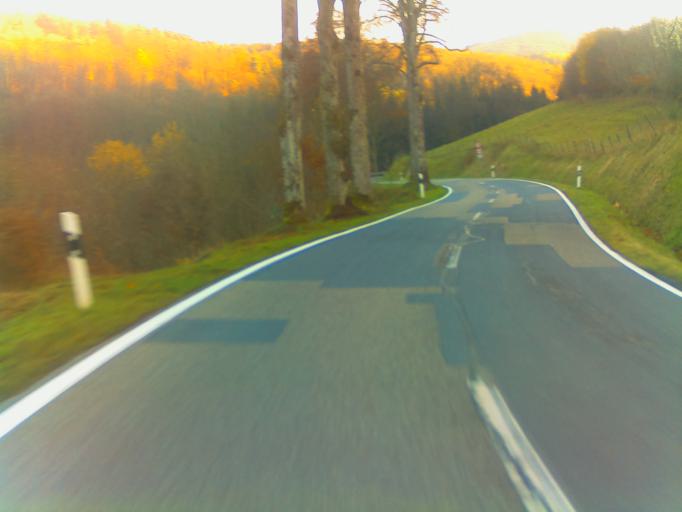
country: DE
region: Hesse
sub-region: Regierungsbezirk Darmstadt
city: Hesseneck
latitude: 49.5528
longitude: 9.0828
